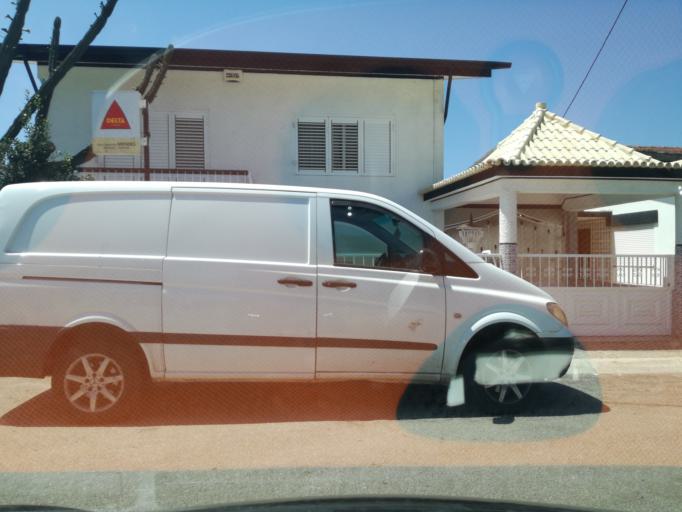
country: PT
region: Porto
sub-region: Maia
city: Maia
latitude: 41.2451
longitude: -8.6238
